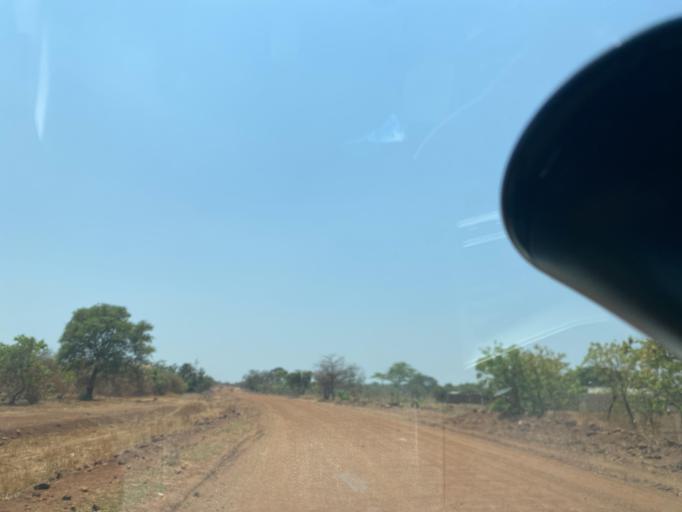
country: ZM
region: Lusaka
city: Lusaka
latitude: -15.4534
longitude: 27.9478
